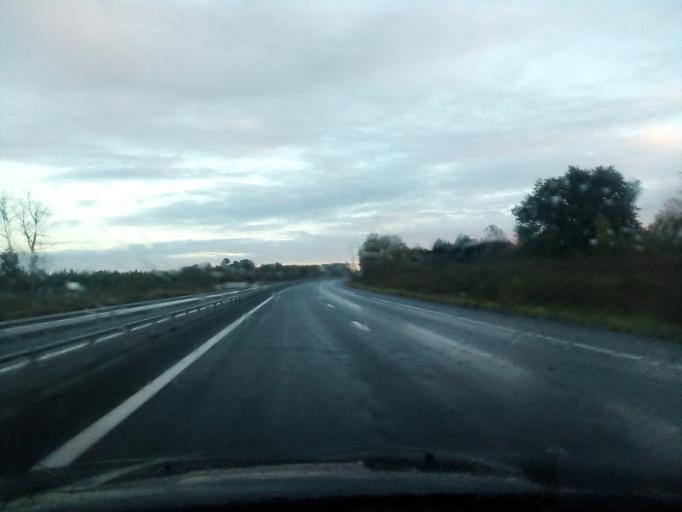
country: FR
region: Aquitaine
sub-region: Departement de la Gironde
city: Saint-Mariens
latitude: 45.1255
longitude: -0.3747
